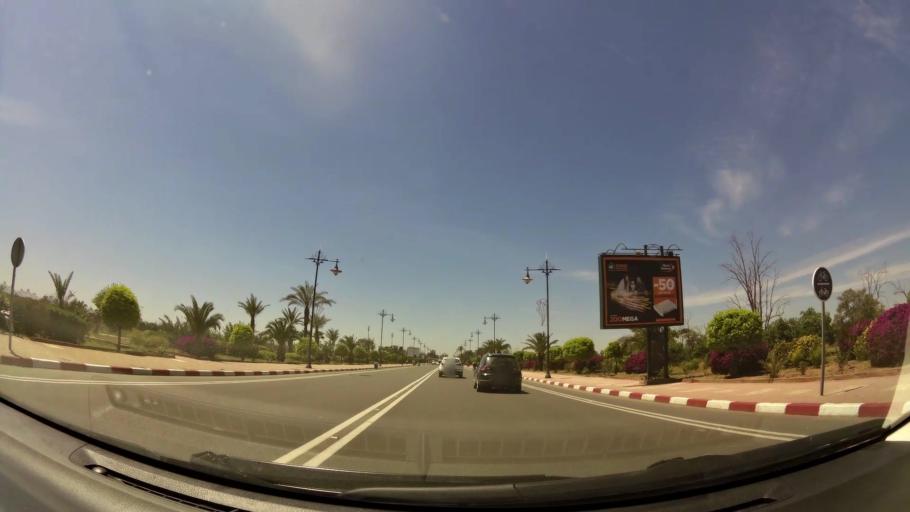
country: MA
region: Marrakech-Tensift-Al Haouz
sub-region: Marrakech
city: Marrakesh
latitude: 31.6155
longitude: -8.0137
